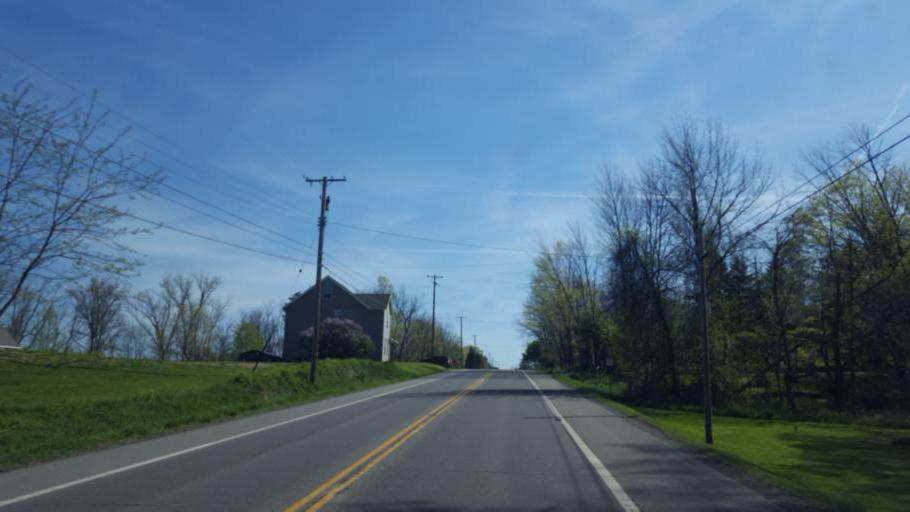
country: US
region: Ohio
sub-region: Ashland County
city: Ashland
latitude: 40.8301
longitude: -82.3782
